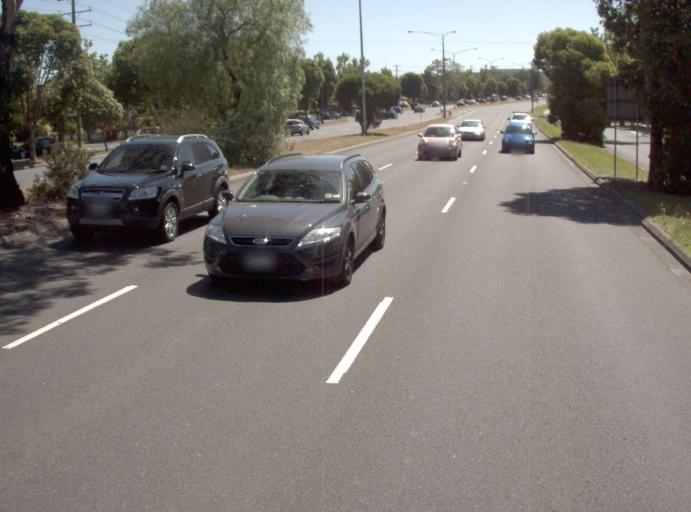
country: AU
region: Victoria
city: Carnegie
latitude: -37.8846
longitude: 145.0658
